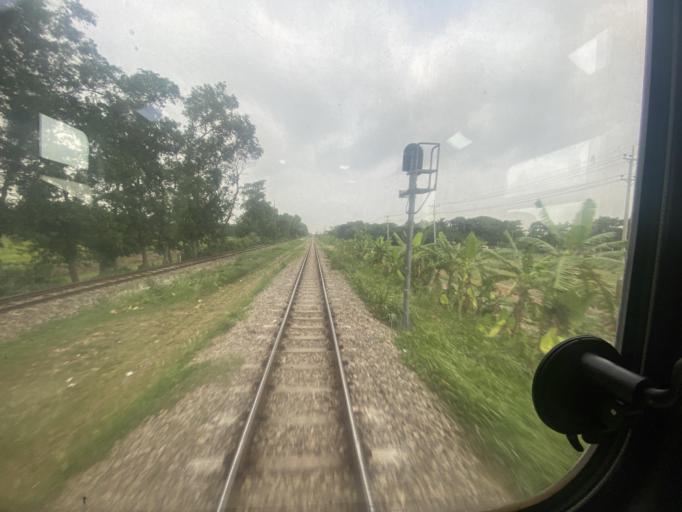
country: BD
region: Dhaka
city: Tungi
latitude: 23.9327
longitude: 90.5138
